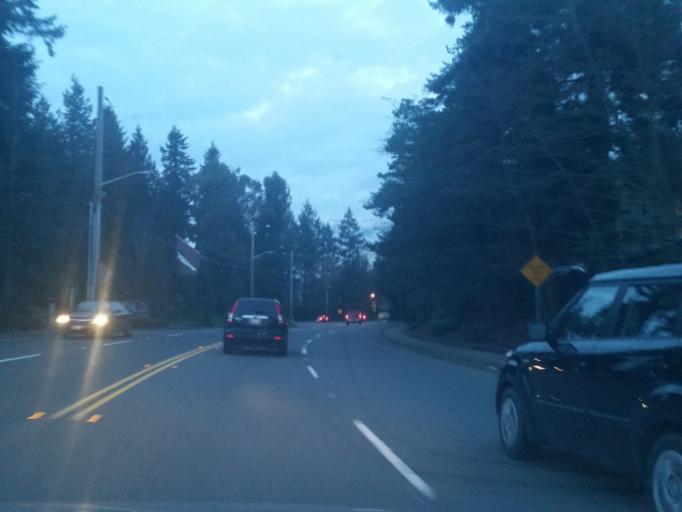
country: US
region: Washington
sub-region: Snohomish County
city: Mountlake Terrace
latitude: 47.7601
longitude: -122.3134
